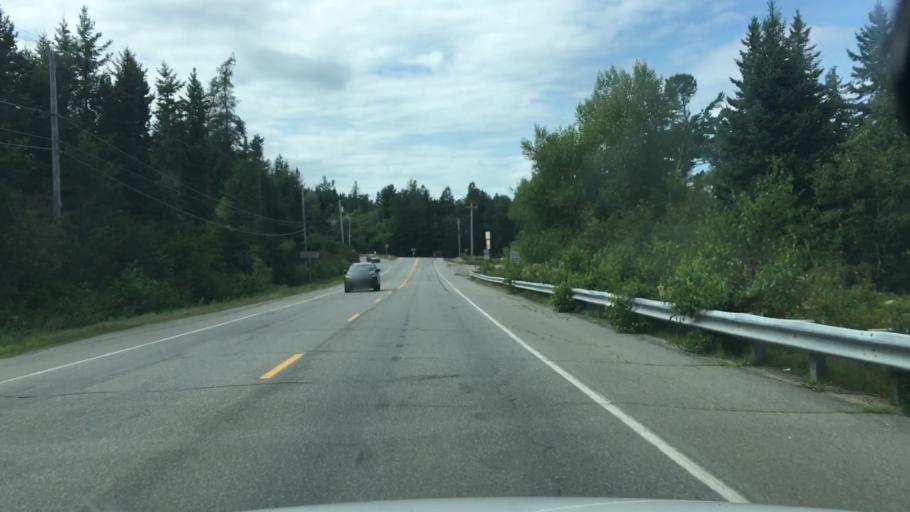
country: US
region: Maine
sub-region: Washington County
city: Eastport
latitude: 44.9693
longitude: -67.0728
